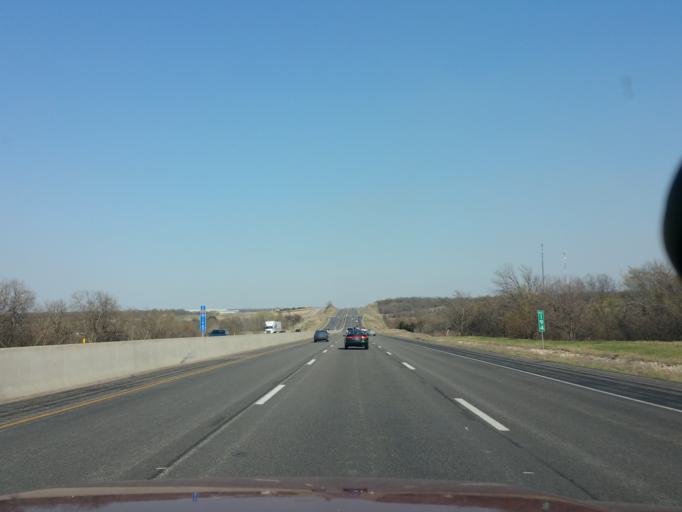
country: US
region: Kansas
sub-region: Douglas County
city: Lawrence
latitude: 39.0000
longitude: -95.4034
